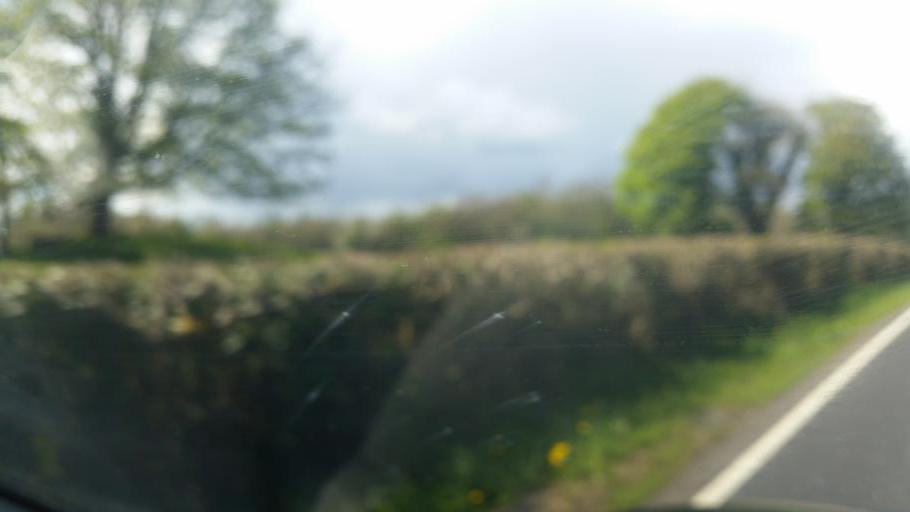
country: GB
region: Northern Ireland
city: Irvinestown
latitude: 54.4386
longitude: -7.7931
